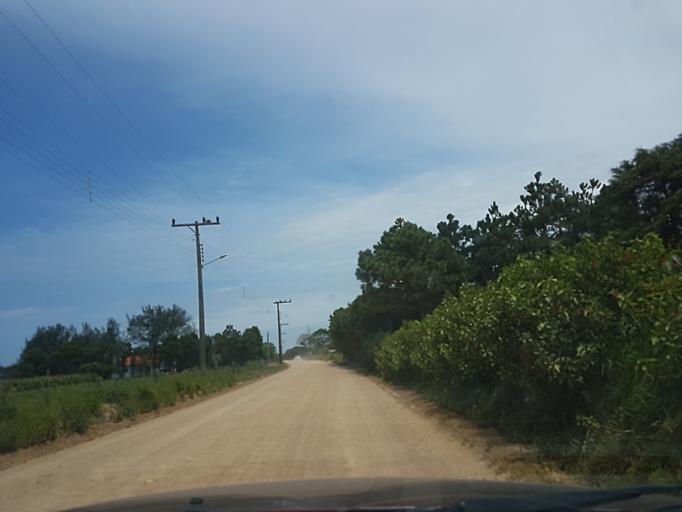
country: BR
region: Santa Catarina
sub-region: Jaguaruna
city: Jaguaruna
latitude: -28.6390
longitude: -48.9615
